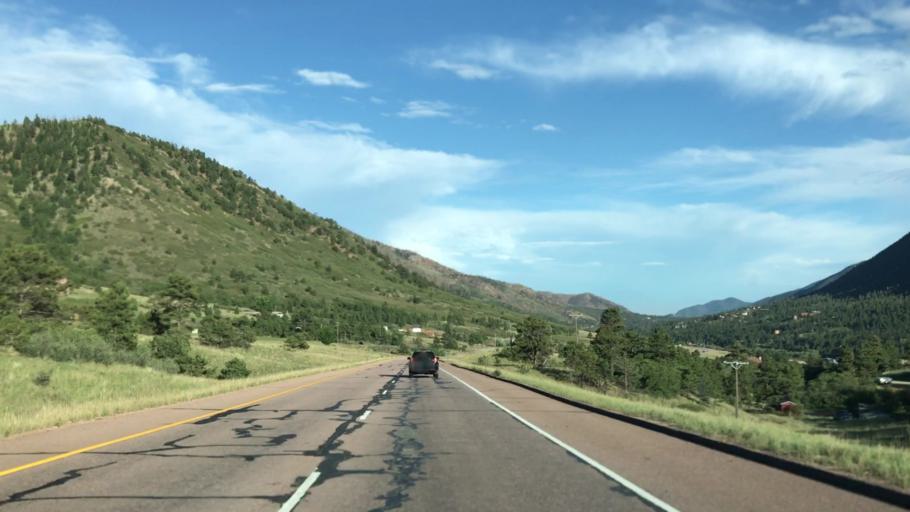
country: US
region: Colorado
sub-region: El Paso County
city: Cascade-Chipita Park
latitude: 38.9330
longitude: -105.0045
